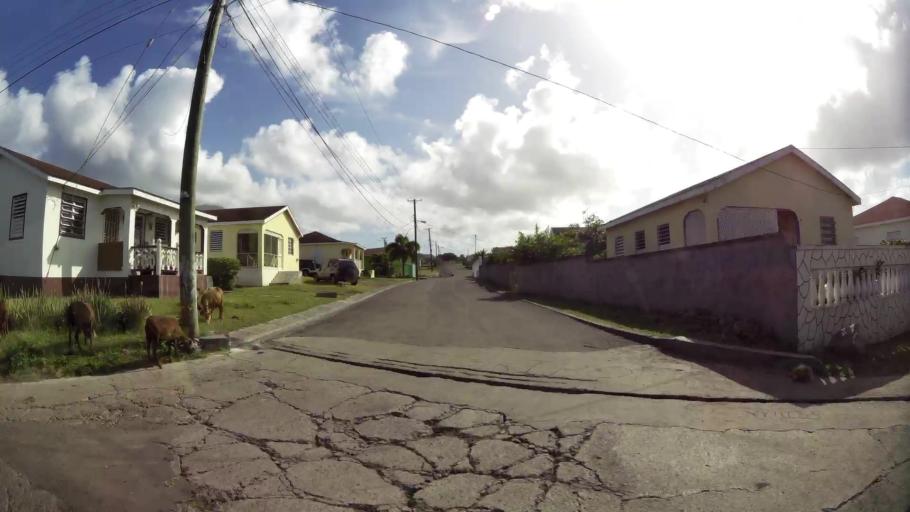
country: KN
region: Saint Paul Charlestown
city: Charlestown
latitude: 17.1277
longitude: -62.6267
